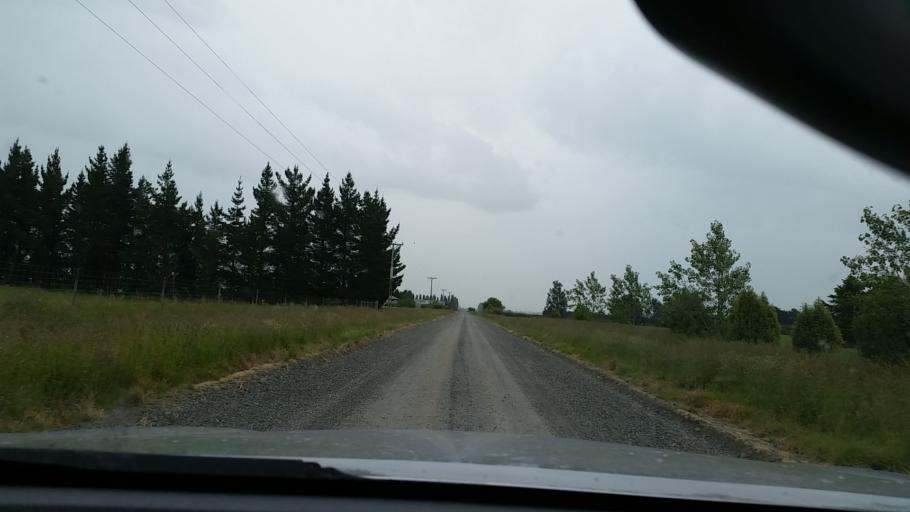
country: NZ
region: Southland
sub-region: Southland District
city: Winton
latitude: -46.0065
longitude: 168.1533
